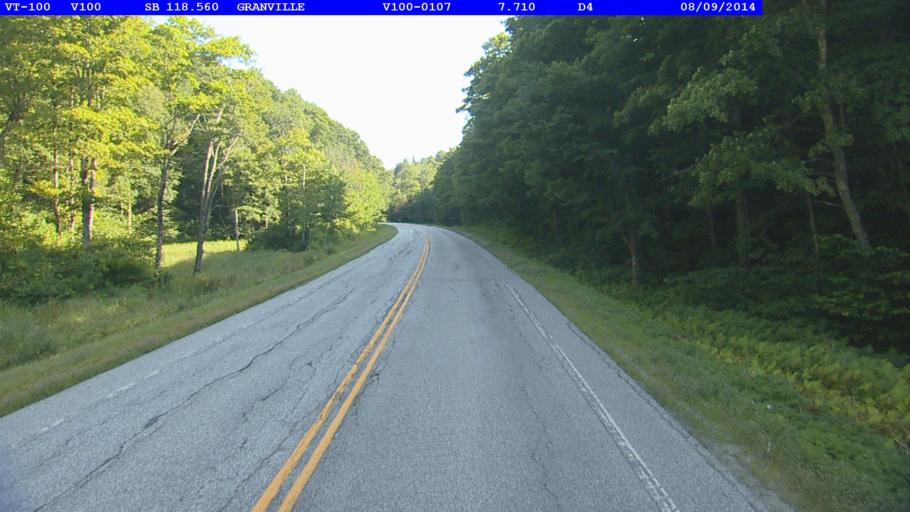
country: US
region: Vermont
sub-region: Orange County
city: Randolph
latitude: 44.0411
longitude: -72.8326
